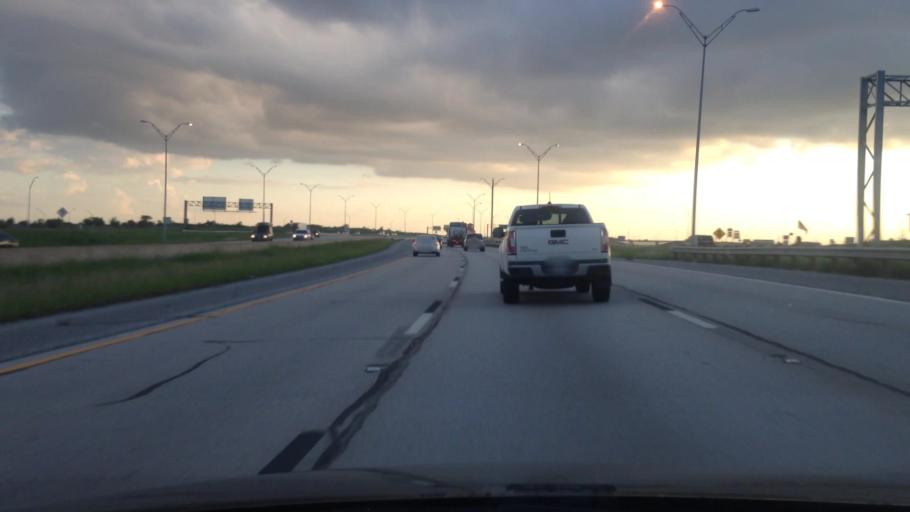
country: US
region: Texas
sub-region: Tarrant County
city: Sansom Park
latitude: 32.8114
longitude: -97.4165
